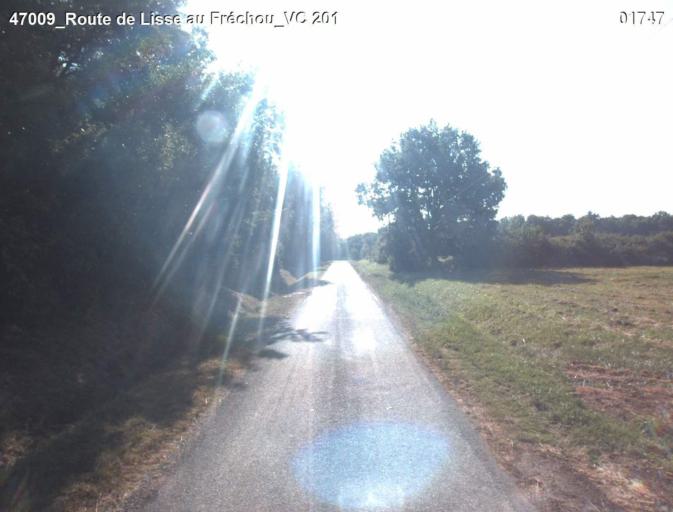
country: FR
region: Aquitaine
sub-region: Departement du Lot-et-Garonne
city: Mezin
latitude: 44.0936
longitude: 0.2908
